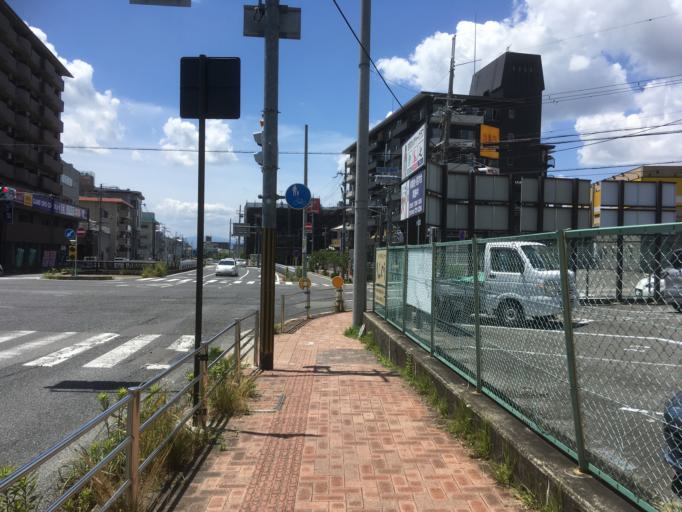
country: JP
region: Nara
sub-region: Ikoma-shi
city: Ikoma
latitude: 34.6915
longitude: 135.7087
